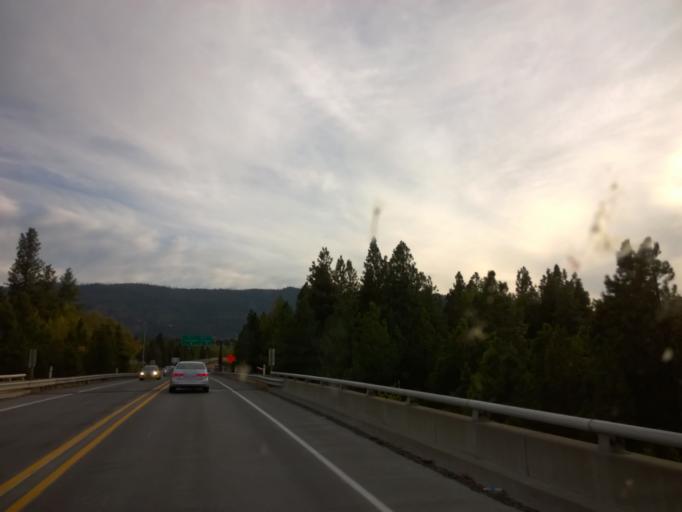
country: US
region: Washington
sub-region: Kittitas County
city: Cle Elum
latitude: 47.1868
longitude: -120.9006
